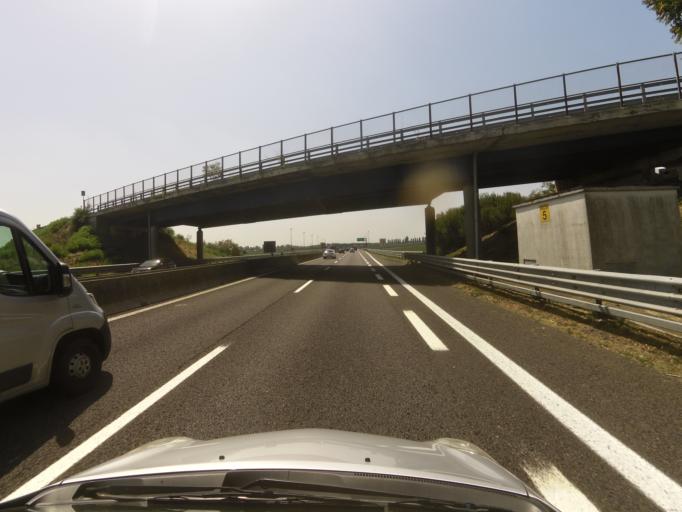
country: IT
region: Emilia-Romagna
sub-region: Provincia di Ferrara
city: Porotto-Cassama
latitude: 44.8703
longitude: 11.5699
